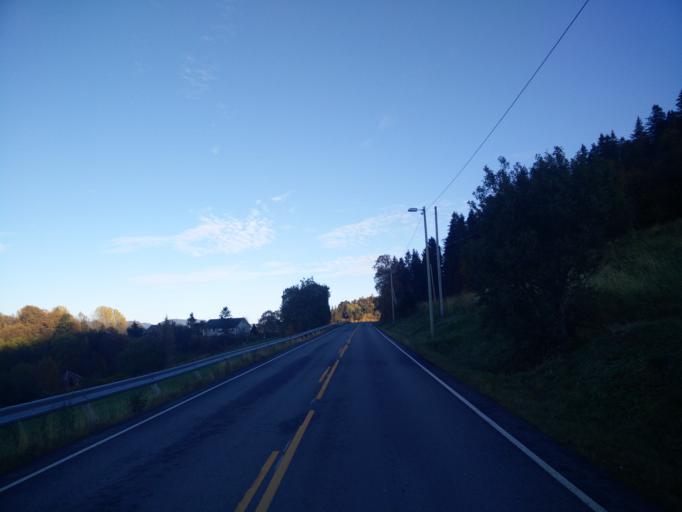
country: NO
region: Sor-Trondelag
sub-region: Skaun
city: Borsa
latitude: 63.3467
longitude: 10.0311
